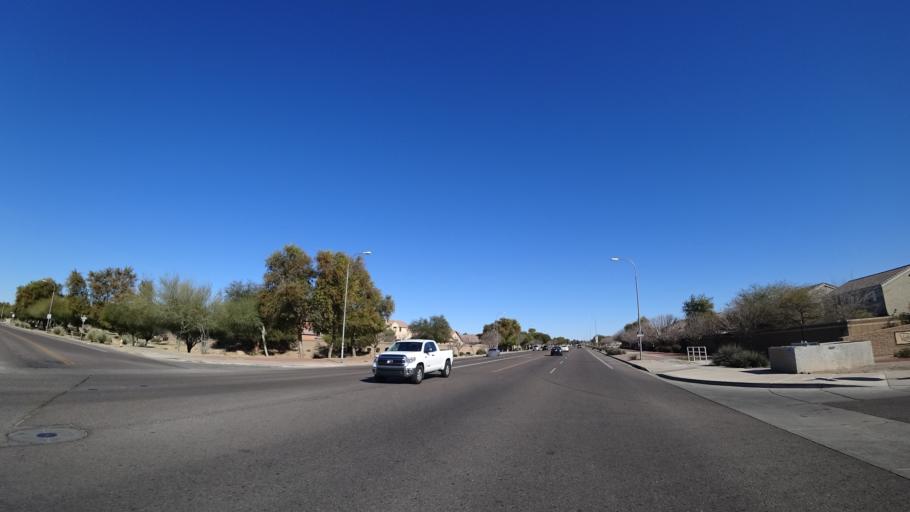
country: US
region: Arizona
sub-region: Maricopa County
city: Tolleson
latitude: 33.4220
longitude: -112.2472
